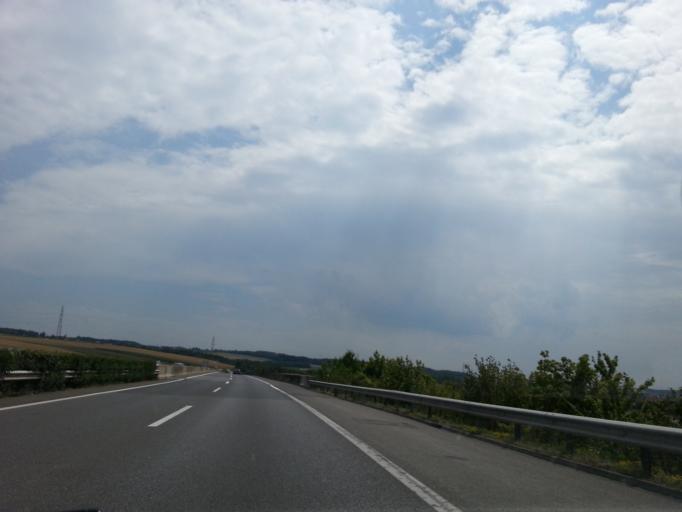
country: CH
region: Vaud
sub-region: Jura-Nord vaudois District
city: Chavornay
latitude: 46.7210
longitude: 6.5717
